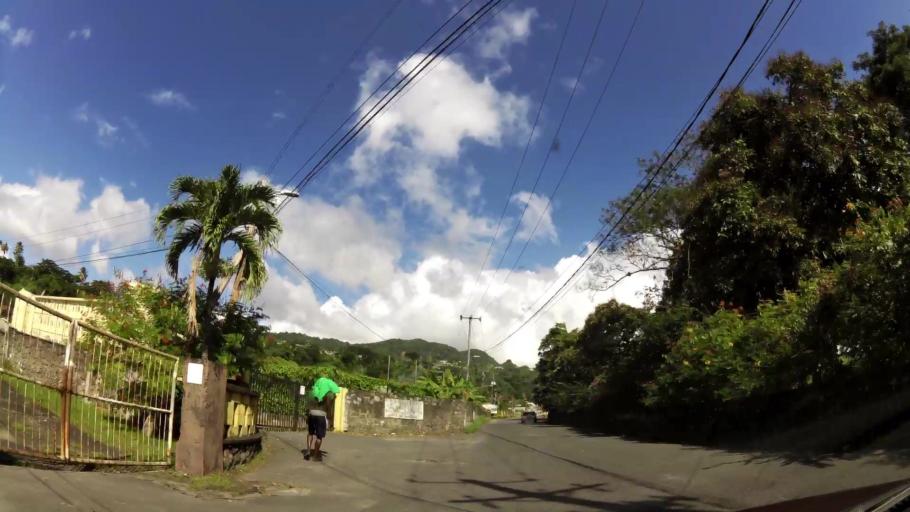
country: DM
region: Saint George
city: Roseau
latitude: 15.3018
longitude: -61.3829
